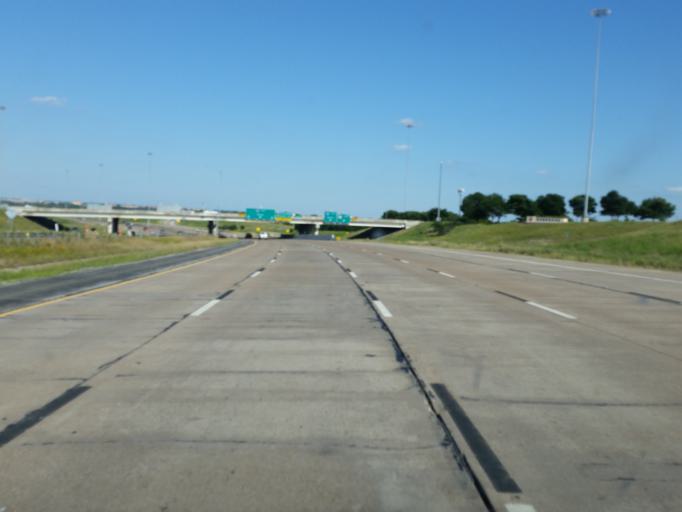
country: US
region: Texas
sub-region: Tarrant County
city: Benbrook
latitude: 32.6852
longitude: -97.4622
